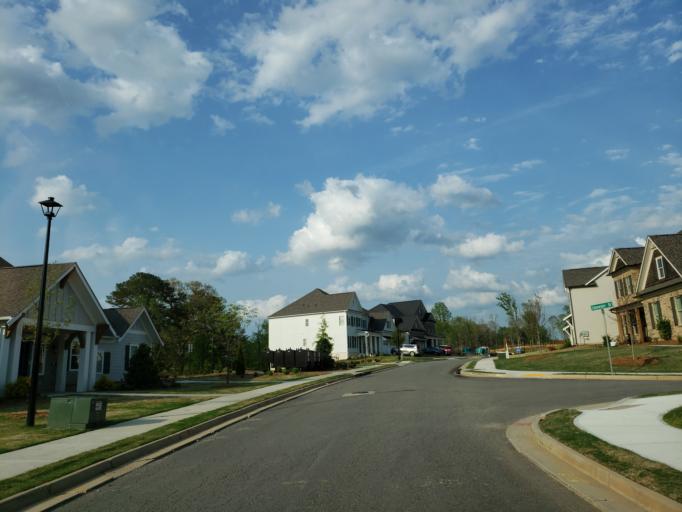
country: US
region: Georgia
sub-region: Cherokee County
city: Holly Springs
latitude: 34.1687
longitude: -84.4351
